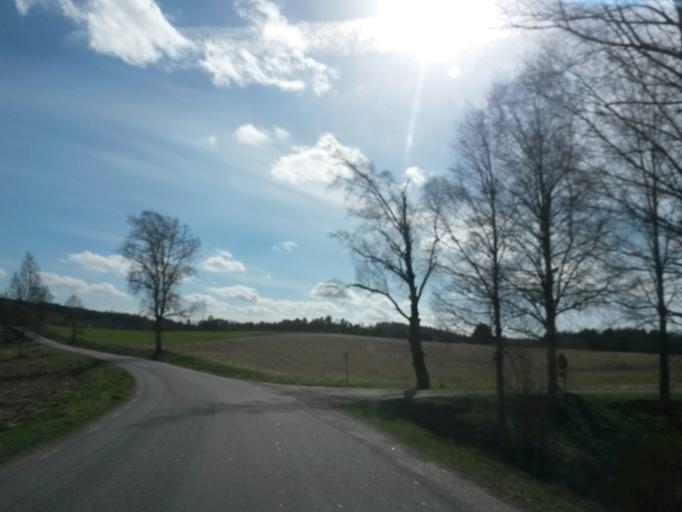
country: SE
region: Vaestra Goetaland
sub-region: Vargarda Kommun
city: Jonstorp
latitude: 57.9431
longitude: 12.7026
